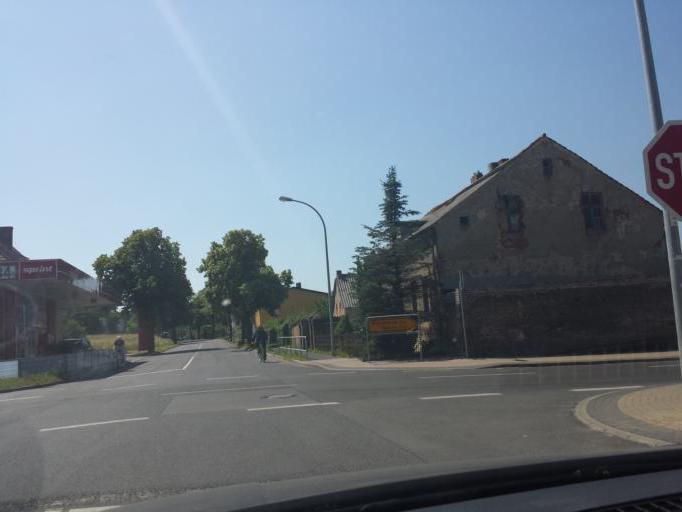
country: DE
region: Brandenburg
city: Rangsdorf
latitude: 52.3436
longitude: 13.4348
